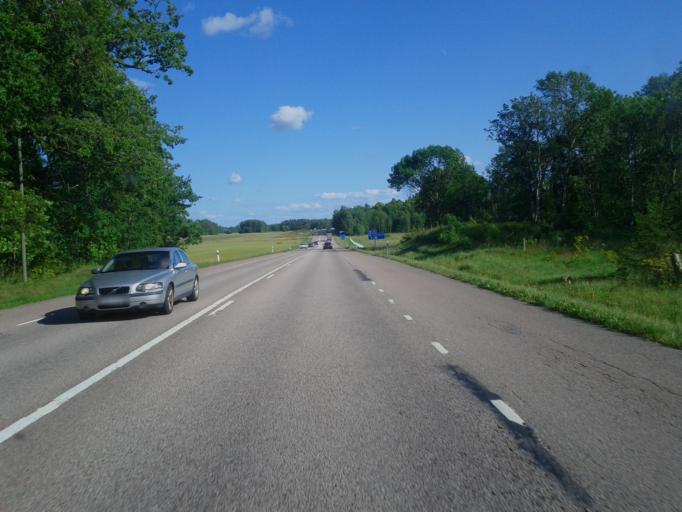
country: SE
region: Uppsala
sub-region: Enkopings Kommun
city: Enkoping
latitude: 59.6731
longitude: 17.0568
